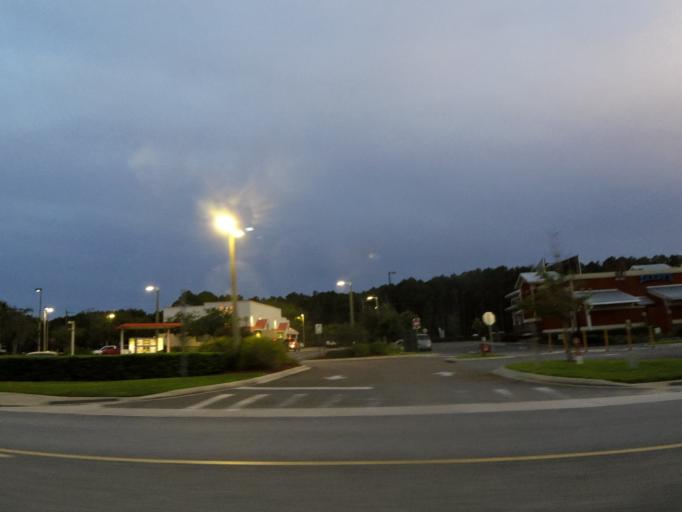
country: US
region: Florida
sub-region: Nassau County
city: Yulee
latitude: 30.6282
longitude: -81.5508
